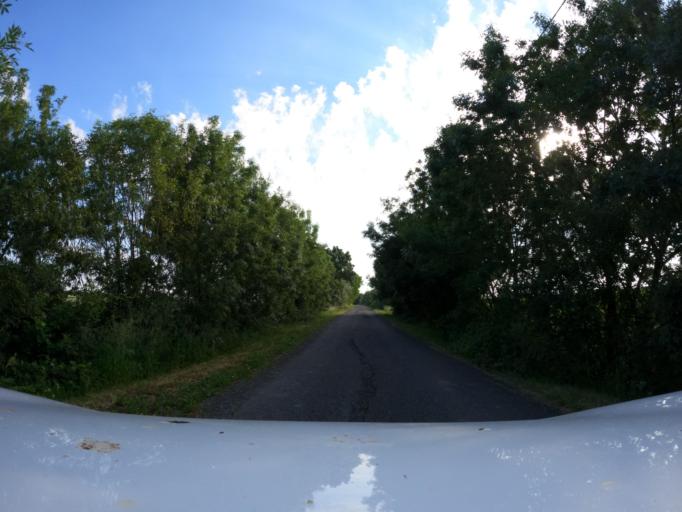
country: FR
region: Pays de la Loire
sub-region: Departement de la Vendee
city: Champagne-les-Marais
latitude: 46.3618
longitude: -1.0853
